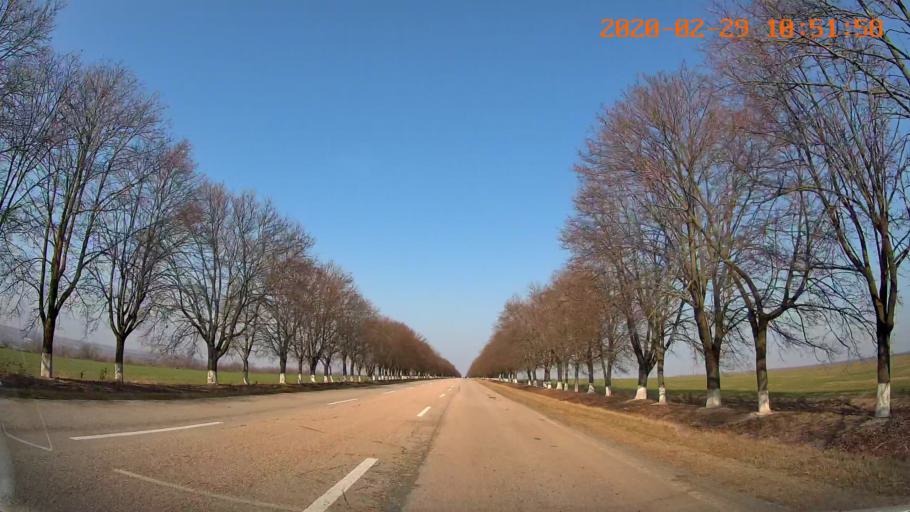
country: MD
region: Telenesti
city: Grigoriopol
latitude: 47.0993
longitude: 29.3568
